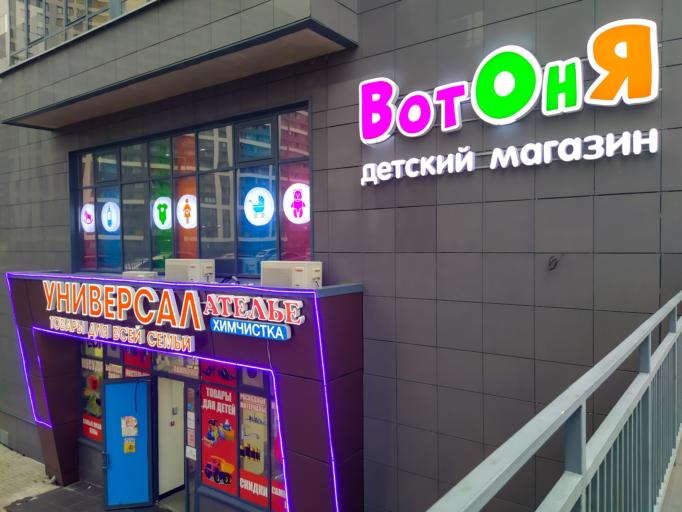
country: RU
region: Leningrad
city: Murino
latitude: 60.0531
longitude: 30.4393
